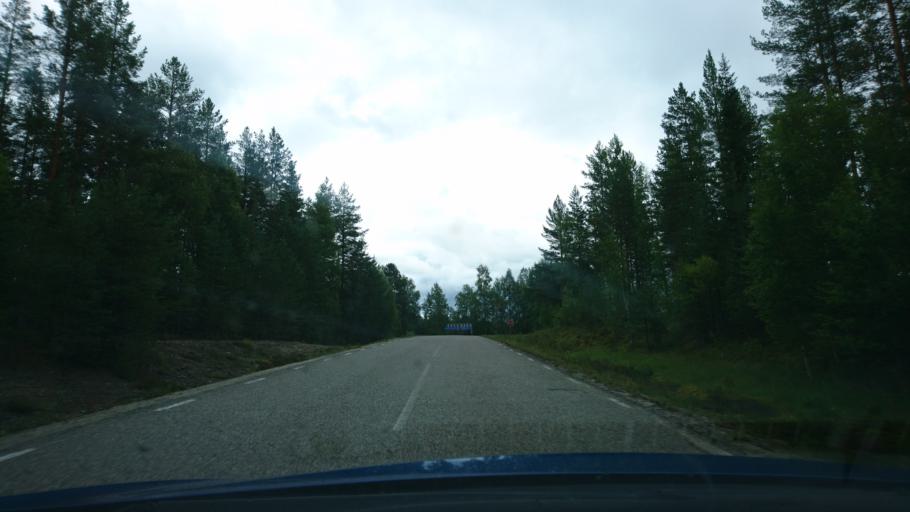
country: SE
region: Vaesterbotten
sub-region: Norsjo Kommun
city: Norsjoe
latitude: 64.5791
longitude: 19.3016
